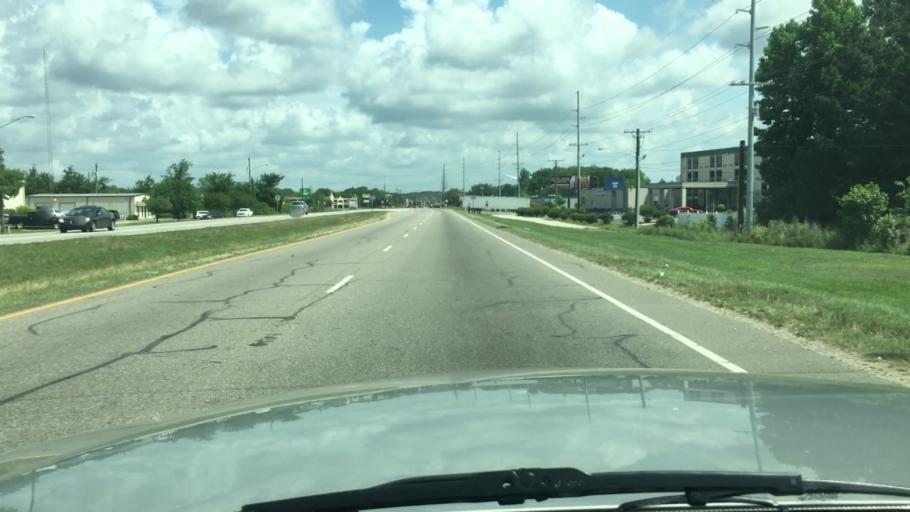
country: US
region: North Carolina
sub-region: Cumberland County
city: Fayetteville
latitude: 35.0402
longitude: -78.8663
